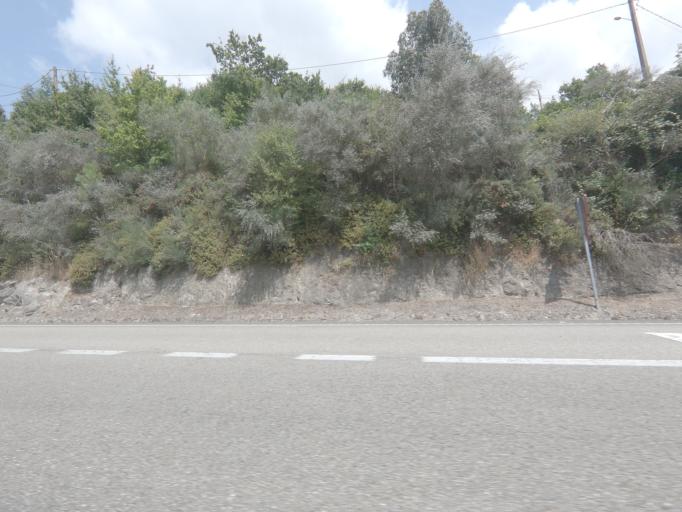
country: ES
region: Galicia
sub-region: Provincia de Pontevedra
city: Tomino
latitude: 42.0427
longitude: -8.7287
